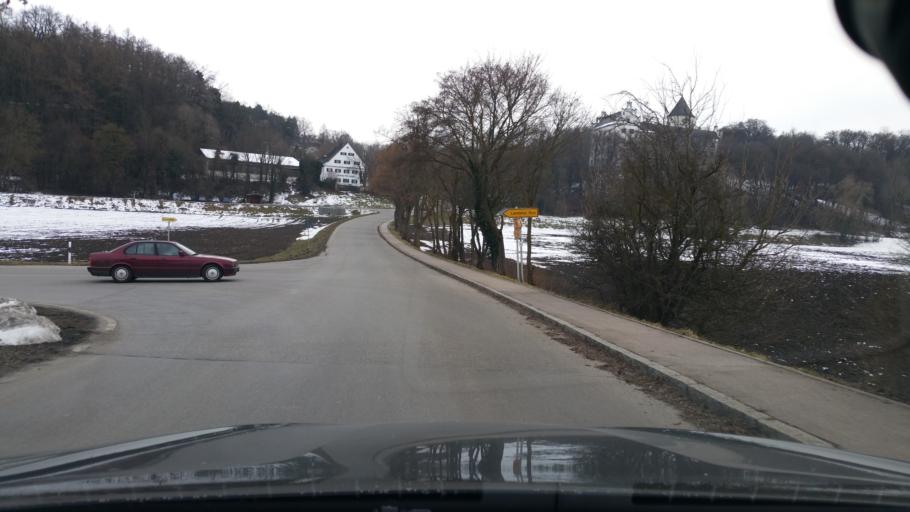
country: DE
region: Bavaria
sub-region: Lower Bavaria
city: Eching
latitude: 48.4955
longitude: 12.0387
